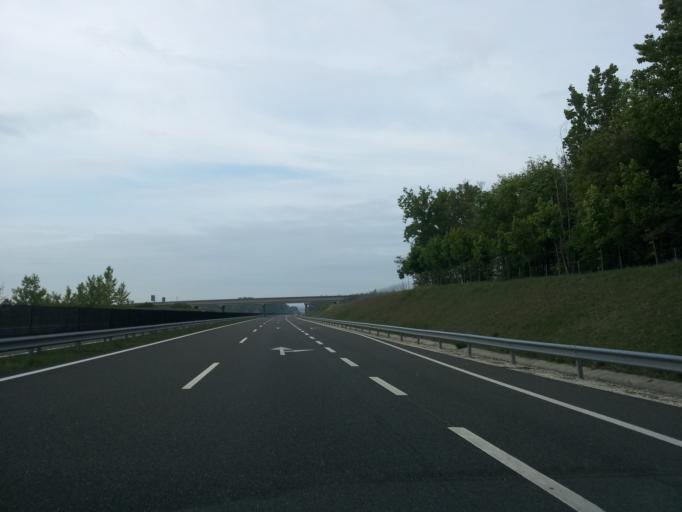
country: HU
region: Fejer
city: Baracs
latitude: 46.8585
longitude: 18.8758
